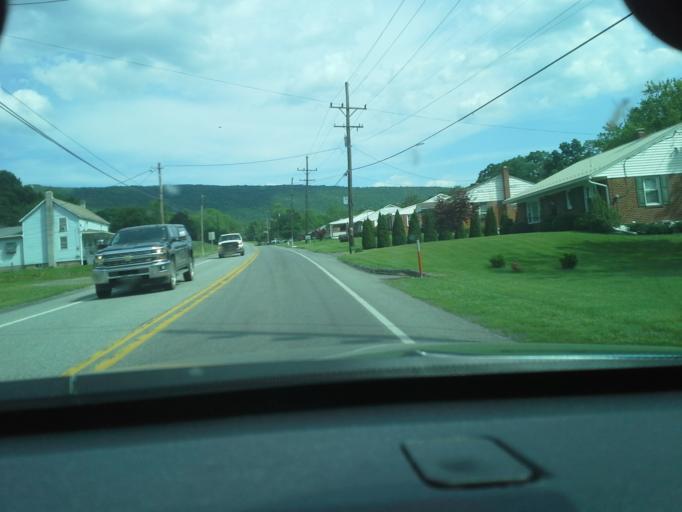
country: US
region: Pennsylvania
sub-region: Fulton County
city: McConnellsburg
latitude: 39.9233
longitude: -77.9831
